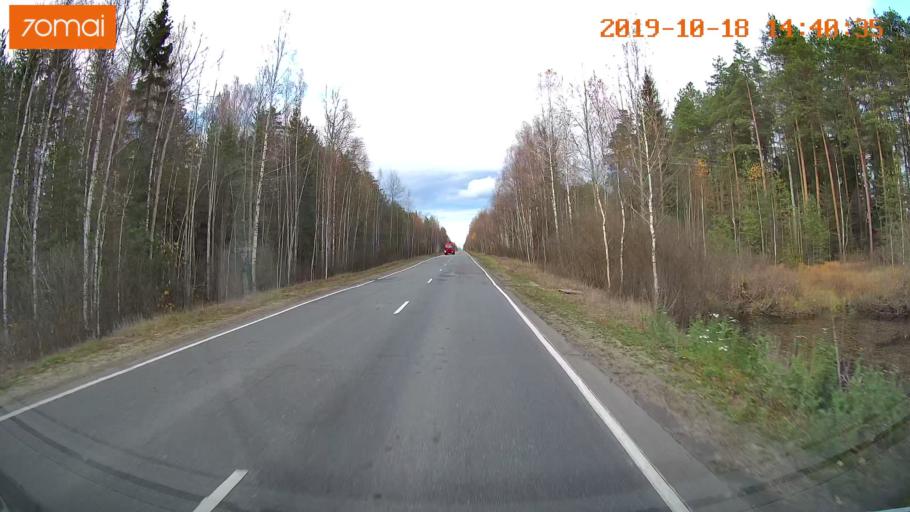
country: RU
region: Vladimir
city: Velikodvorskiy
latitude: 55.2790
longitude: 40.6693
